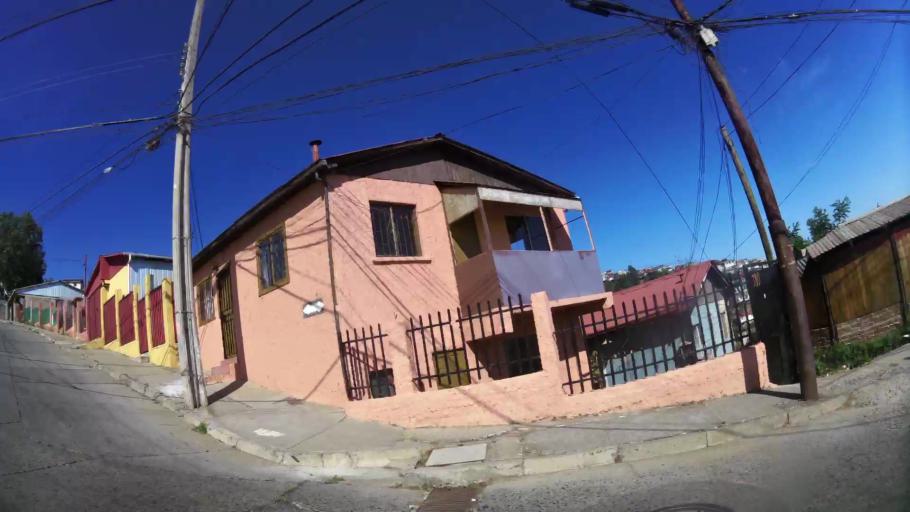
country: CL
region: Valparaiso
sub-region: Provincia de Valparaiso
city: Valparaiso
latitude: -33.0489
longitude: -71.6376
